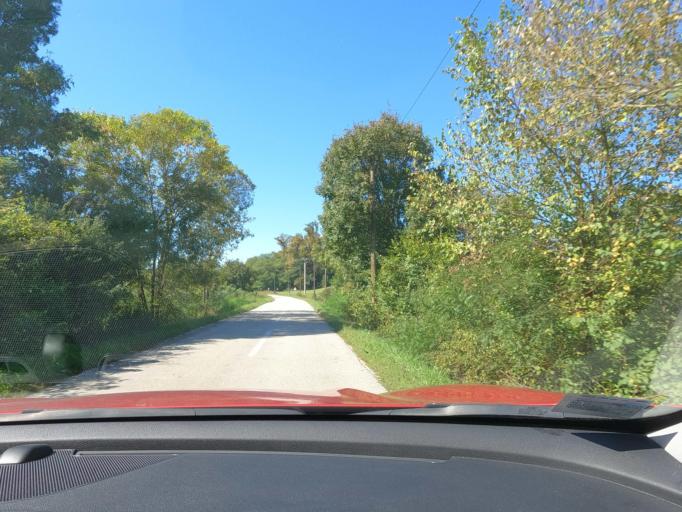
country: HR
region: Sisacko-Moslavacka
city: Petrinja
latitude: 45.4698
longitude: 16.3105
